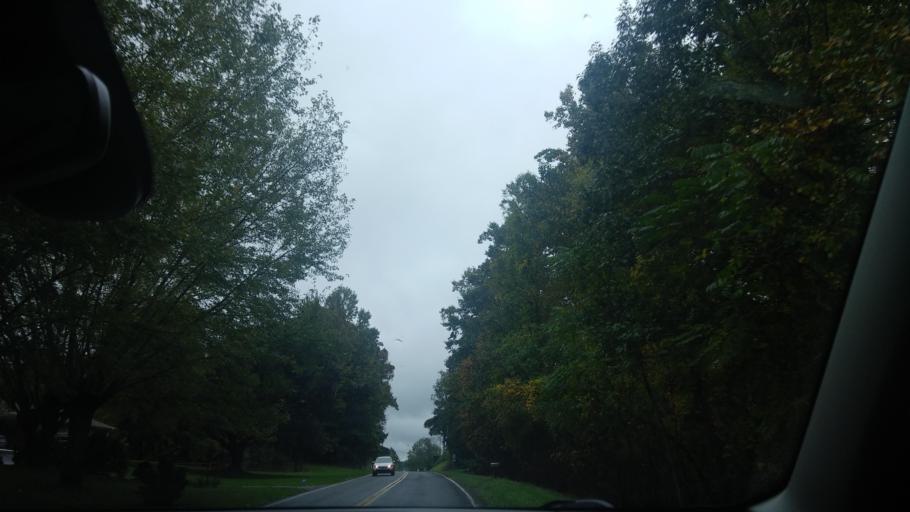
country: US
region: Virginia
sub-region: City of Galax
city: Galax
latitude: 36.6279
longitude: -80.9210
